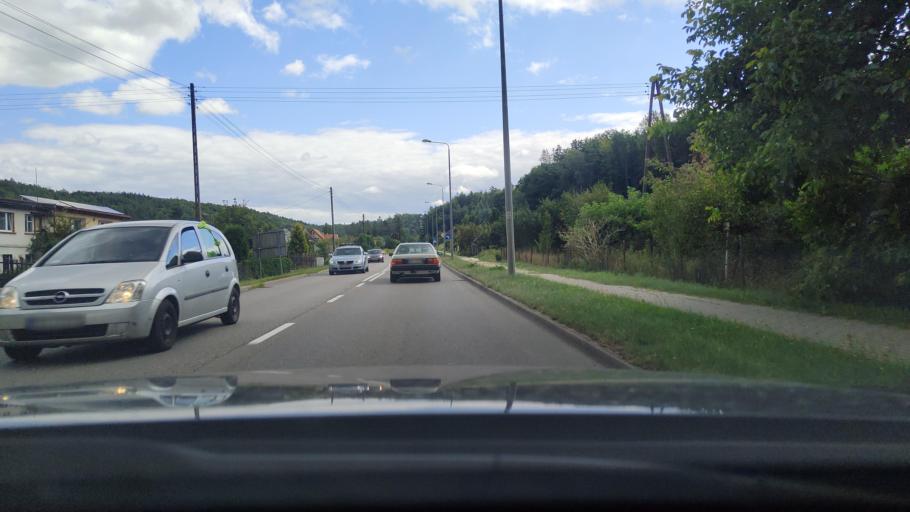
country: PL
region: Pomeranian Voivodeship
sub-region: Powiat wejherowski
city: Wejherowo
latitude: 54.5889
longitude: 18.2455
